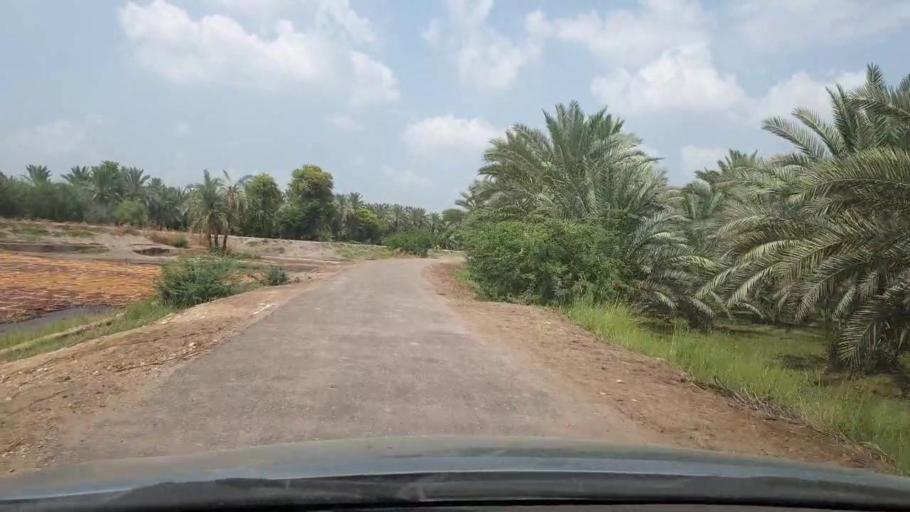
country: PK
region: Sindh
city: Kot Diji
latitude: 27.3949
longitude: 68.7409
